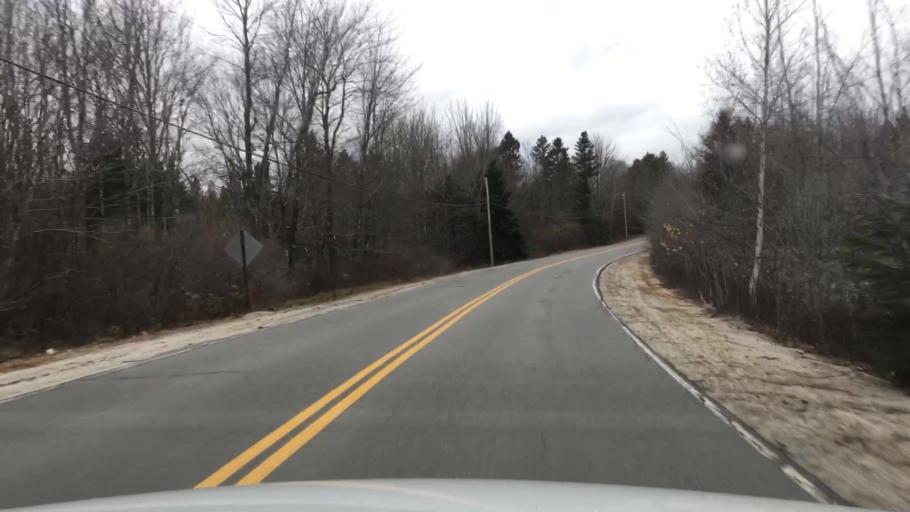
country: US
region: Maine
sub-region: Hancock County
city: Penobscot
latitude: 44.4327
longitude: -68.6302
